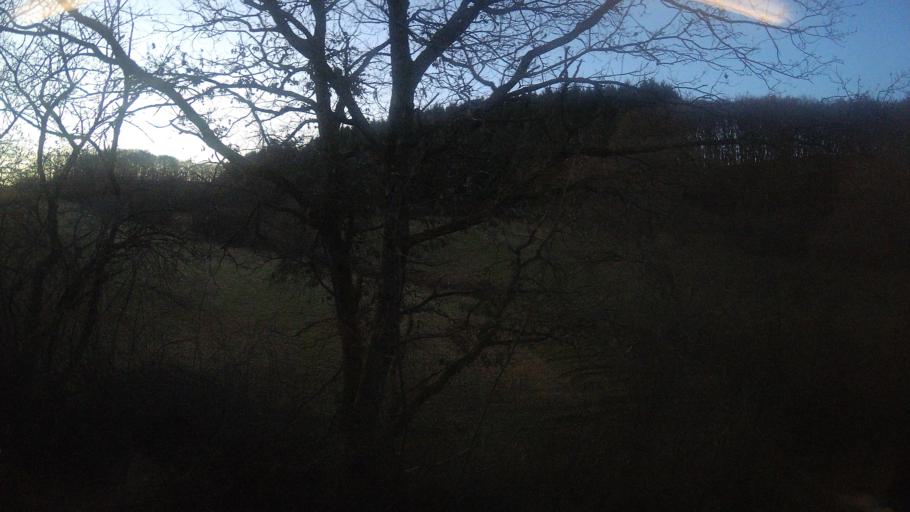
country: DE
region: Rheinland-Pfalz
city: Herchweiler
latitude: 49.5025
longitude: 7.2639
